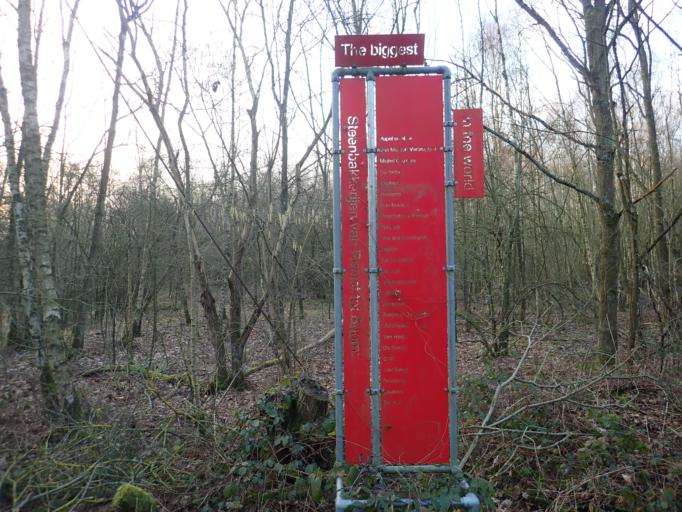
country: BE
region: Flanders
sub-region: Provincie Antwerpen
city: Boom
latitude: 51.0883
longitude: 4.3872
